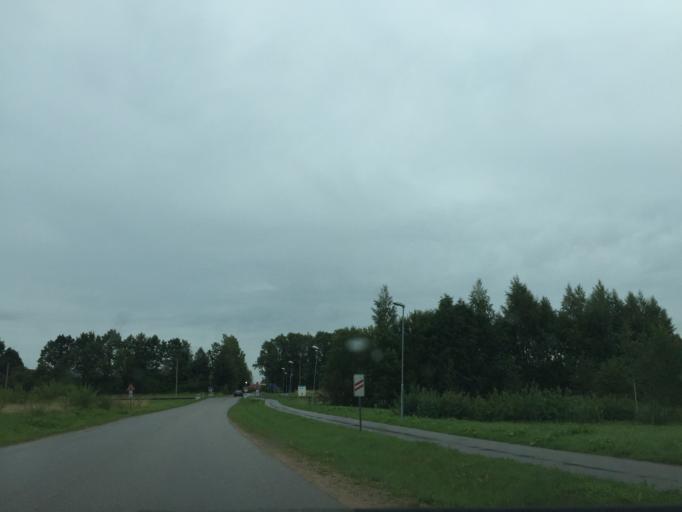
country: LV
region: Livani
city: Livani
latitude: 56.3903
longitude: 26.1541
